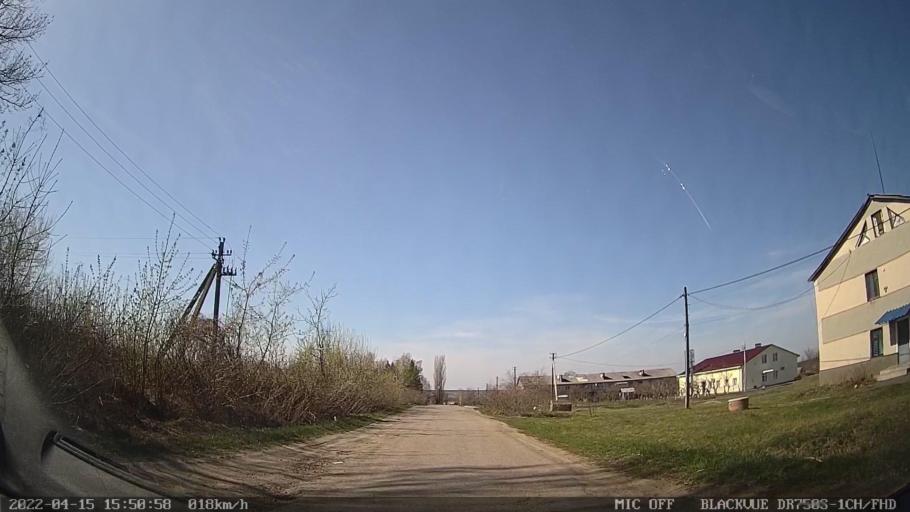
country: MD
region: Raionul Ocnita
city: Otaci
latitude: 48.3930
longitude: 27.8998
